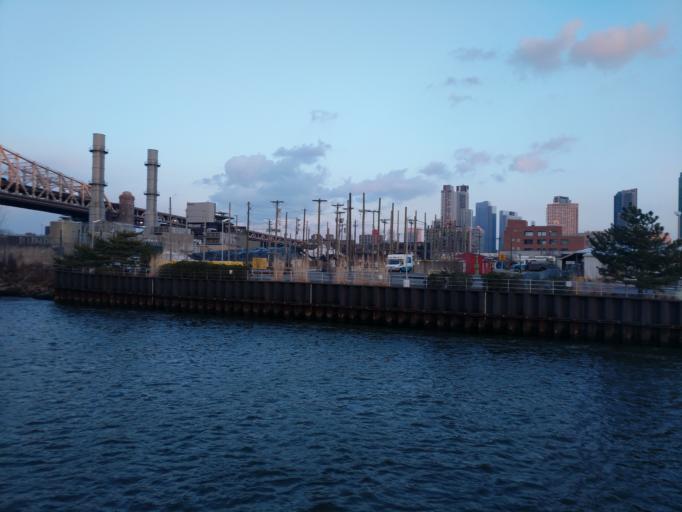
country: US
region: New York
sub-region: Queens County
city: Long Island City
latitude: 40.7535
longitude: -73.9531
